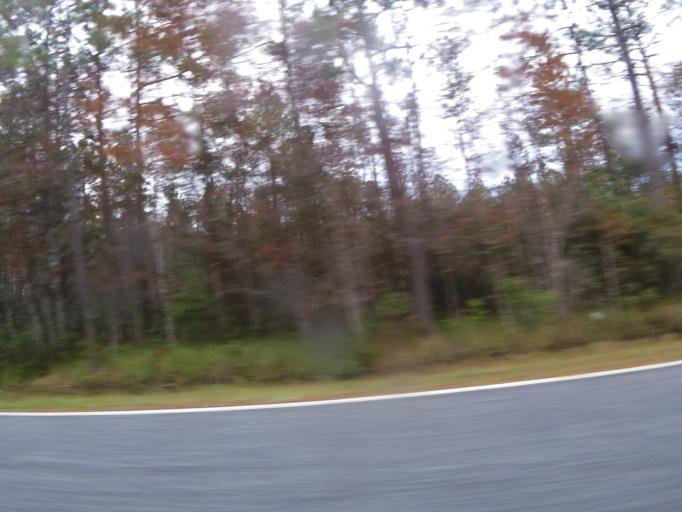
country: US
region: Georgia
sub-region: Charlton County
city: Folkston
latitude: 30.8704
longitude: -82.0432
